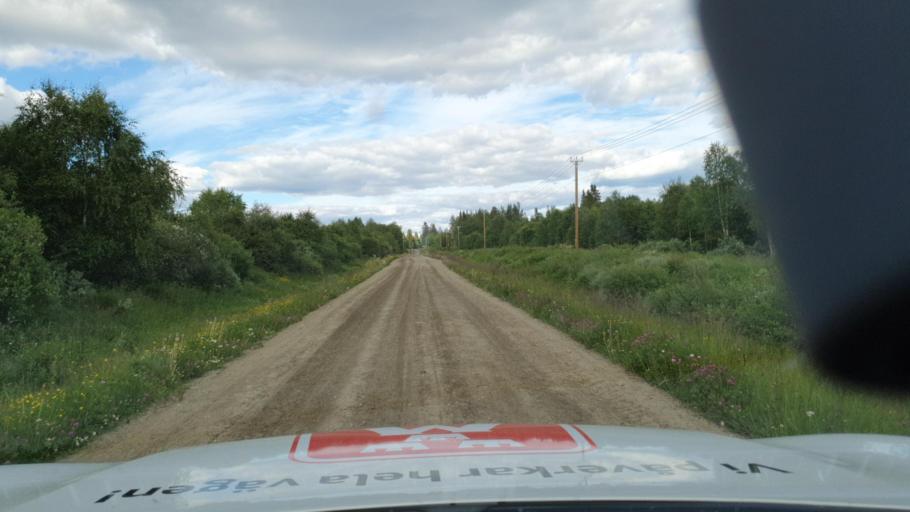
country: SE
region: Vaesterbotten
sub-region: Lycksele Kommun
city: Lycksele
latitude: 64.3195
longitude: 18.3172
